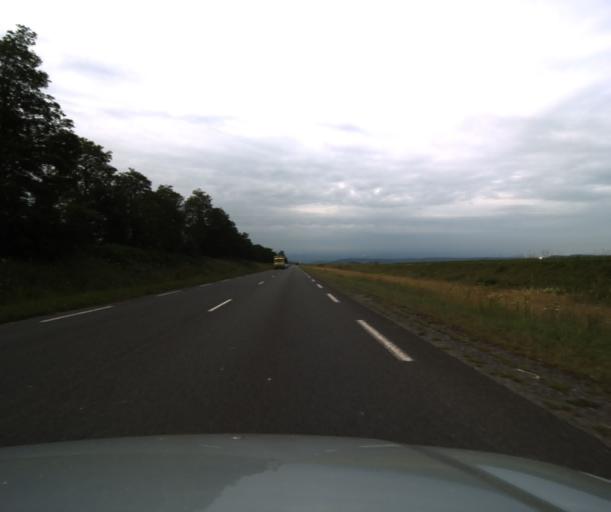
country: FR
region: Midi-Pyrenees
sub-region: Departement des Hautes-Pyrenees
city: Juillan
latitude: 43.2137
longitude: 0.0139
